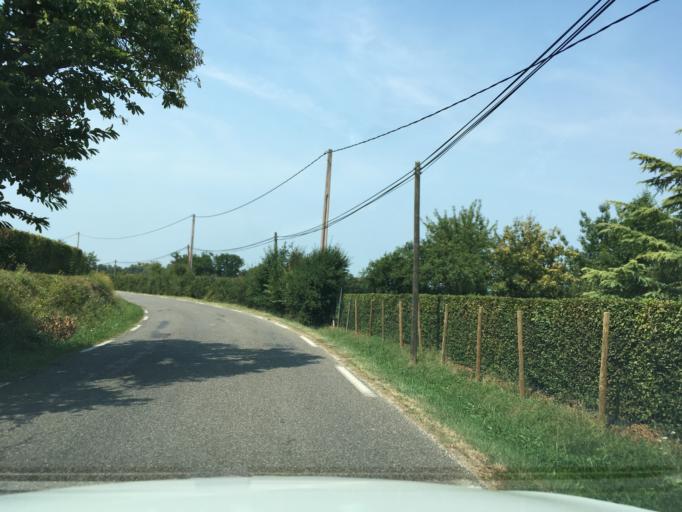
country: FR
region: Midi-Pyrenees
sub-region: Departement du Tarn-et-Garonne
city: Montauban
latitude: 43.9936
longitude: 1.3747
